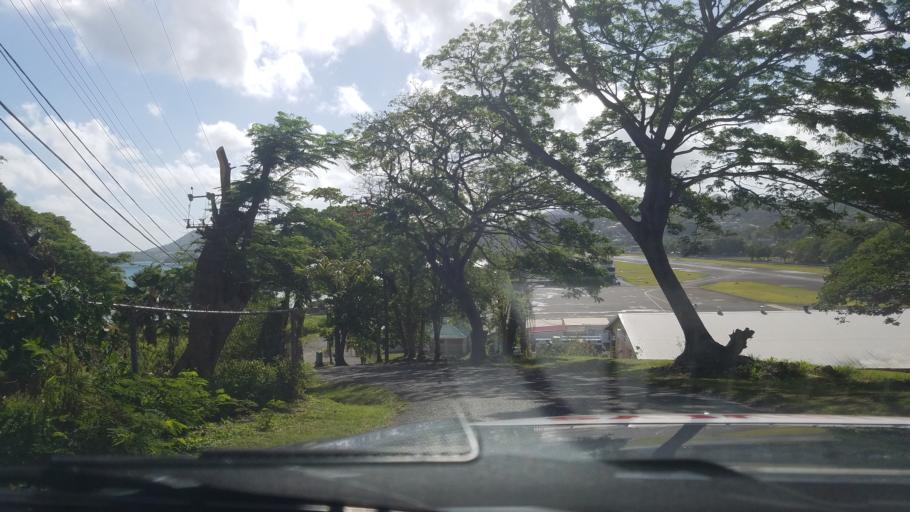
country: LC
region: Castries Quarter
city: Bisee
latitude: 14.0198
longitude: -60.9978
